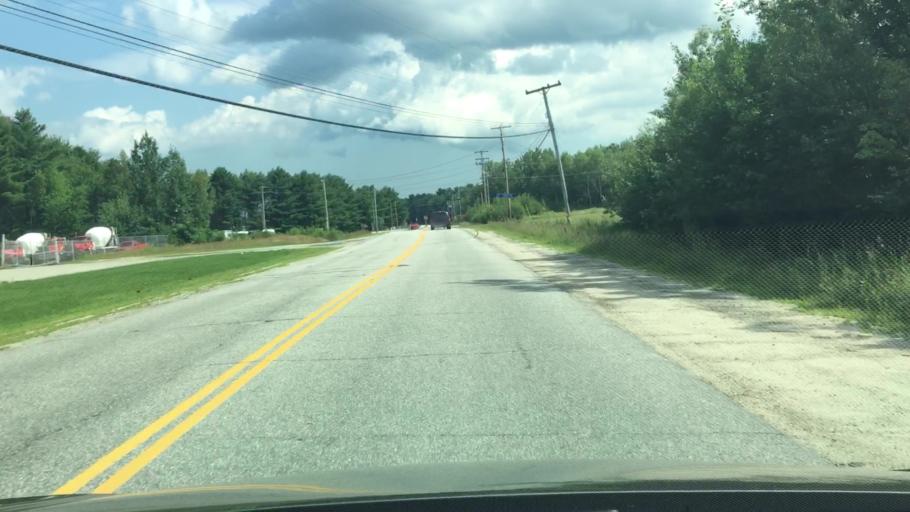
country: US
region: Maine
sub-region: Androscoggin County
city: Auburn
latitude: 44.0757
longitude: -70.2565
